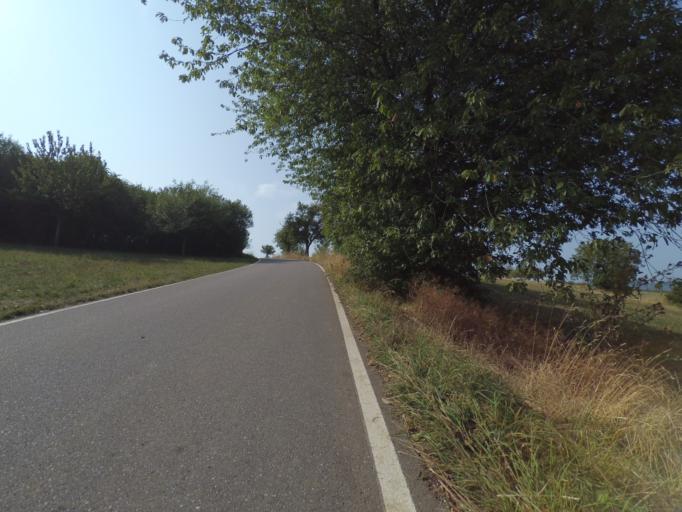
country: DE
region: Saarland
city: Perl
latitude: 49.5118
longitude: 6.4230
